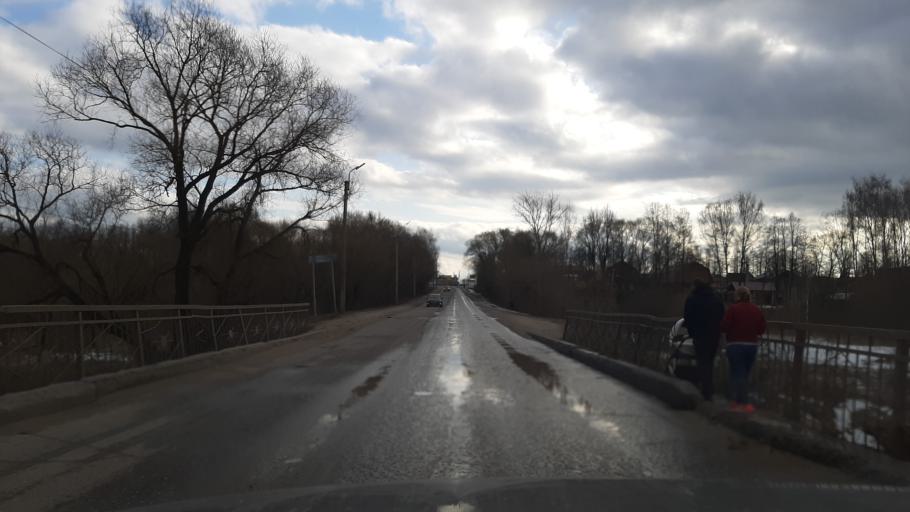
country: RU
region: Ivanovo
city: Teykovo
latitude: 56.8576
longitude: 40.5196
